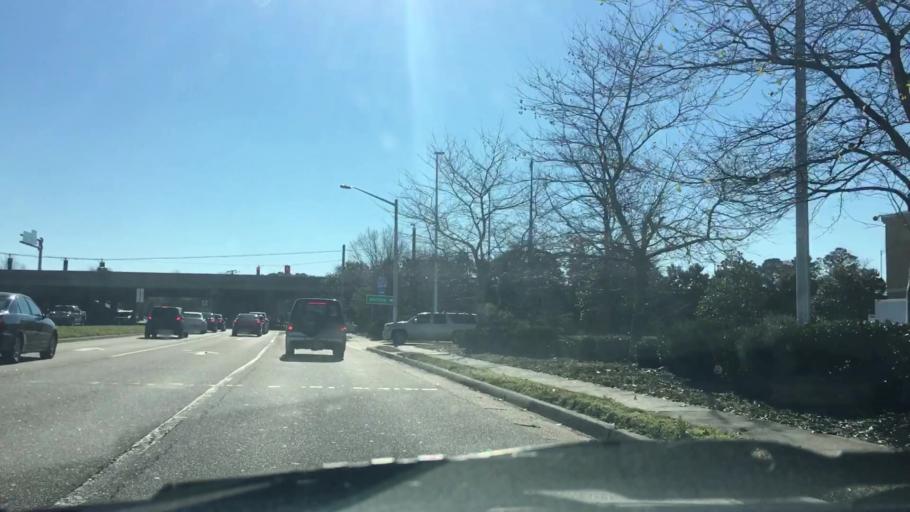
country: US
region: Virginia
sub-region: City of Virginia Beach
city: Virginia Beach
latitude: 36.8468
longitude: -76.0212
